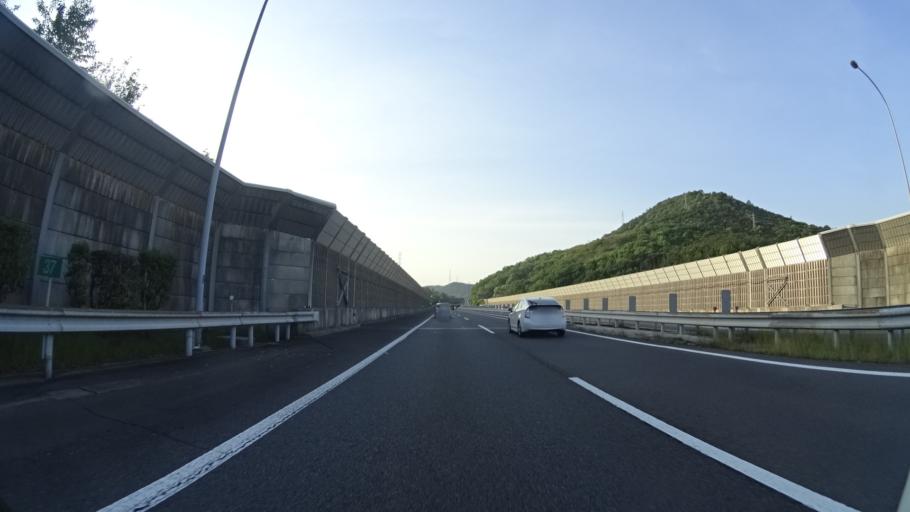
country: JP
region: Kagawa
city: Sakaidecho
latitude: 34.3000
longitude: 133.8426
